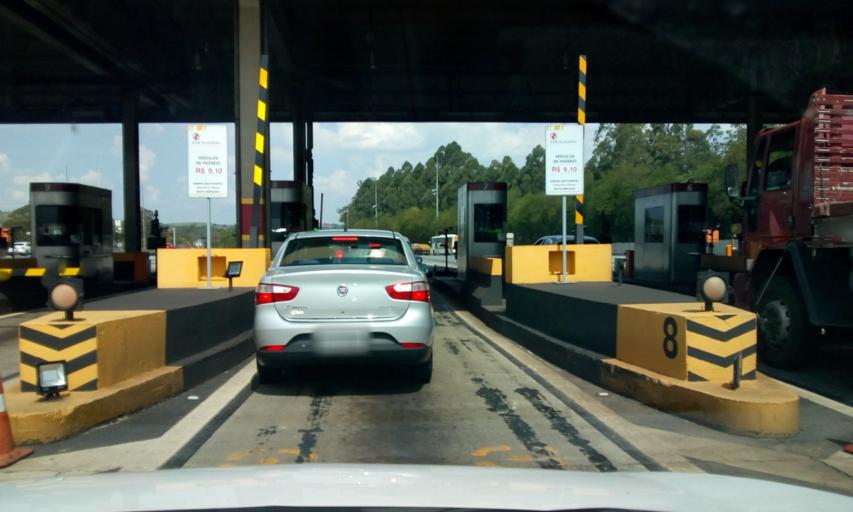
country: BR
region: Sao Paulo
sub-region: Vinhedo
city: Vinhedo
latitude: -23.0580
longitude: -47.0449
